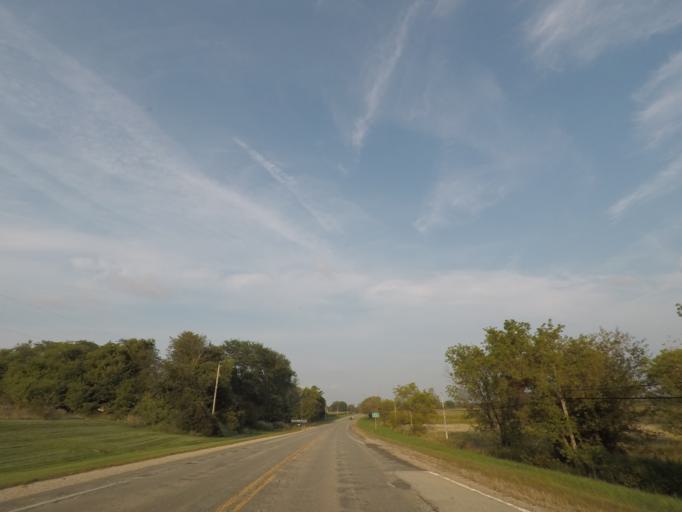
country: US
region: Wisconsin
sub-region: Dane County
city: Cottage Grove
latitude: 43.0878
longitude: -89.2477
